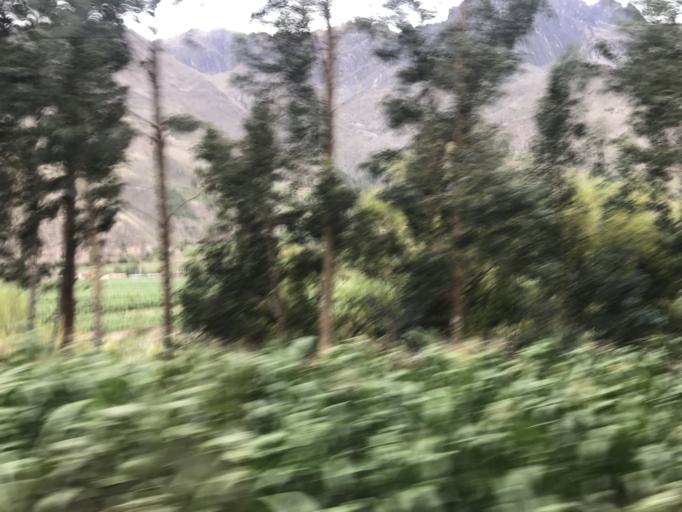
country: PE
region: Cusco
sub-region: Provincia de Urubamba
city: Ollantaytambo
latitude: -13.2510
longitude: -72.2851
